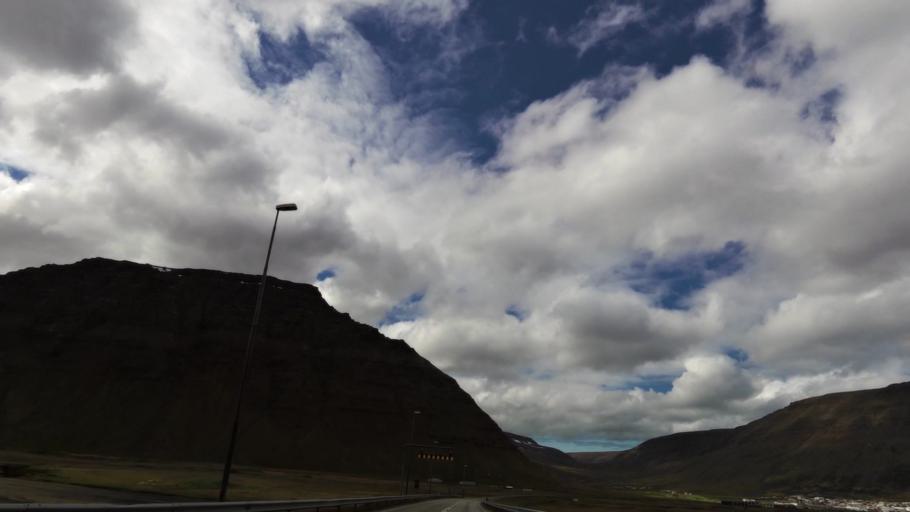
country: IS
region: Westfjords
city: Isafjoerdur
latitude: 66.1435
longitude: -23.2257
